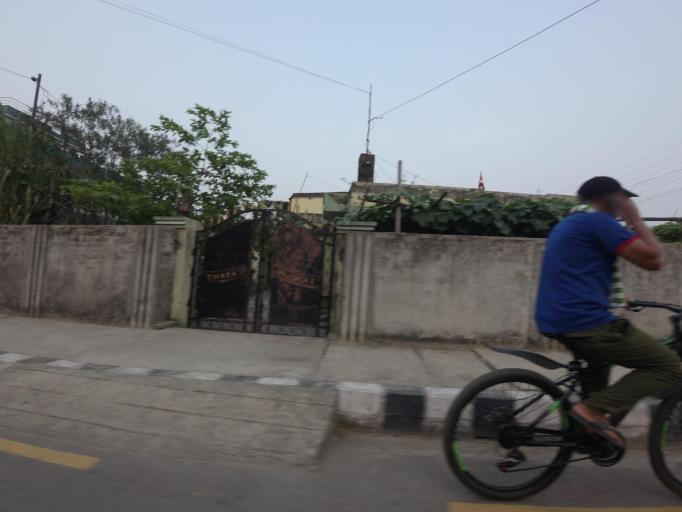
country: NP
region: Western Region
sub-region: Lumbini Zone
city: Bhairahawa
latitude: 27.5031
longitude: 83.4610
